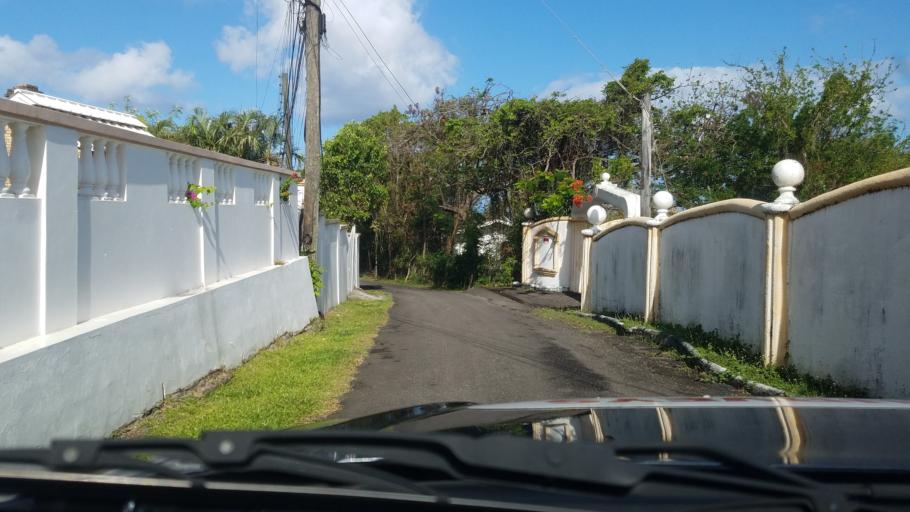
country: LC
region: Castries Quarter
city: Castries
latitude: 14.0227
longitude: -61.0024
